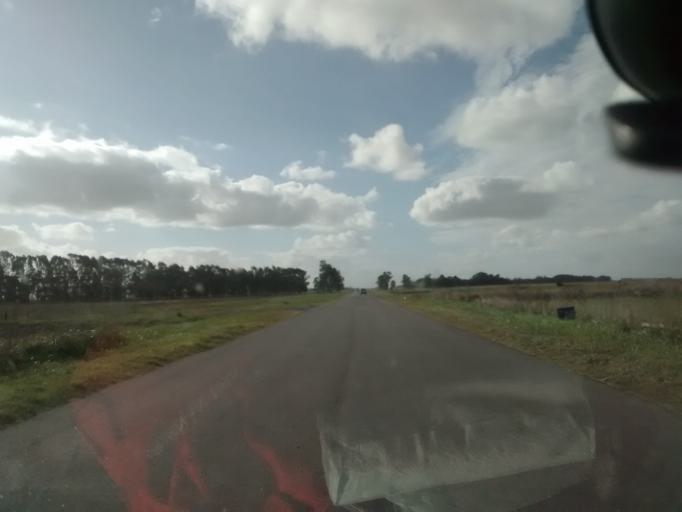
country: AR
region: Buenos Aires
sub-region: Partido de Ayacucho
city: Ayacucho
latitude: -37.2195
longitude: -58.4989
